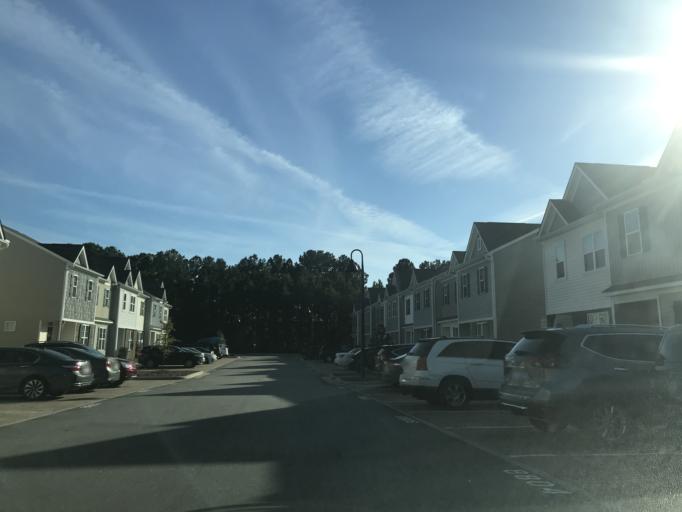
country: US
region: North Carolina
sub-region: Wake County
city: Wake Forest
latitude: 35.8993
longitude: -78.5554
